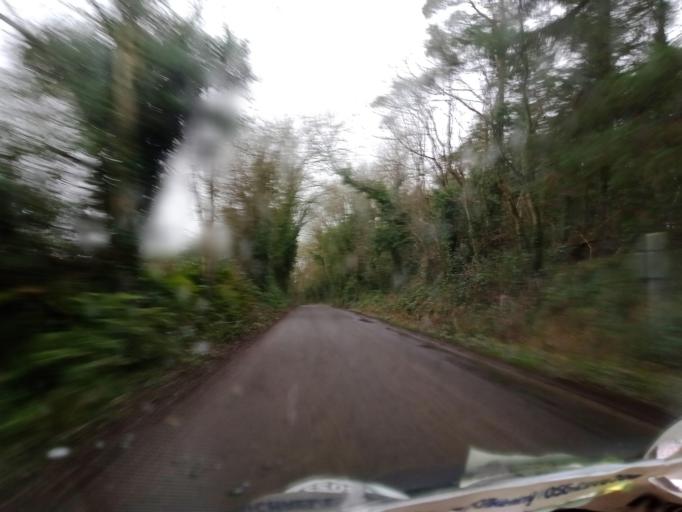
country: IE
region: Munster
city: Fethard
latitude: 52.5522
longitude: -7.7613
